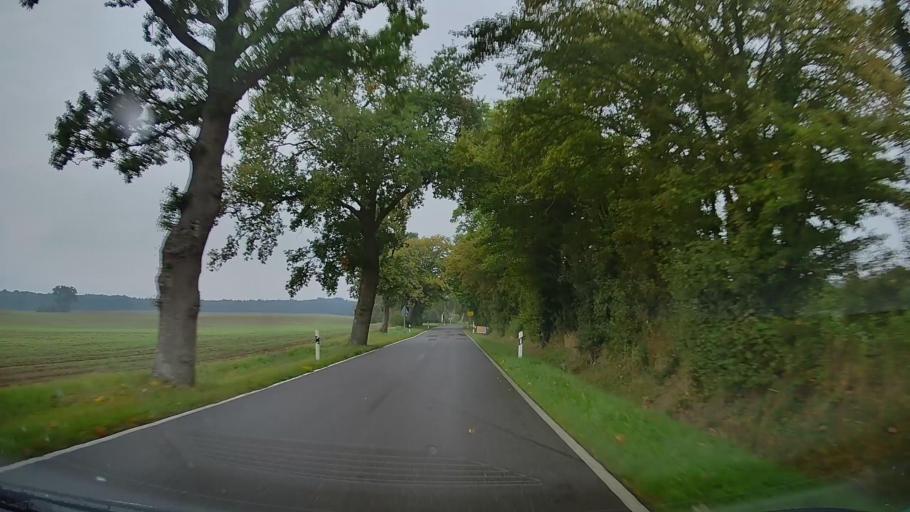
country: DE
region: Mecklenburg-Vorpommern
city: Kalkhorst
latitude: 53.9933
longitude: 11.0433
